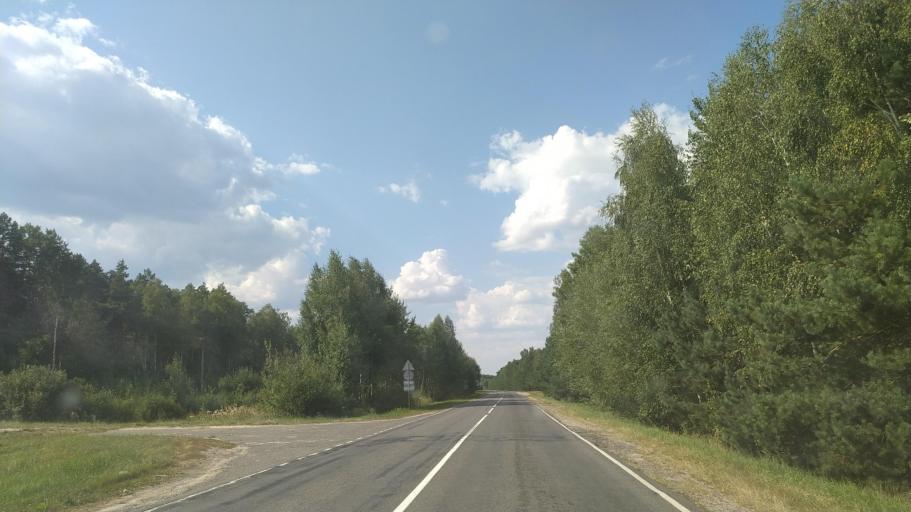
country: BY
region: Brest
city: Drahichyn
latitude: 52.2224
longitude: 25.1233
